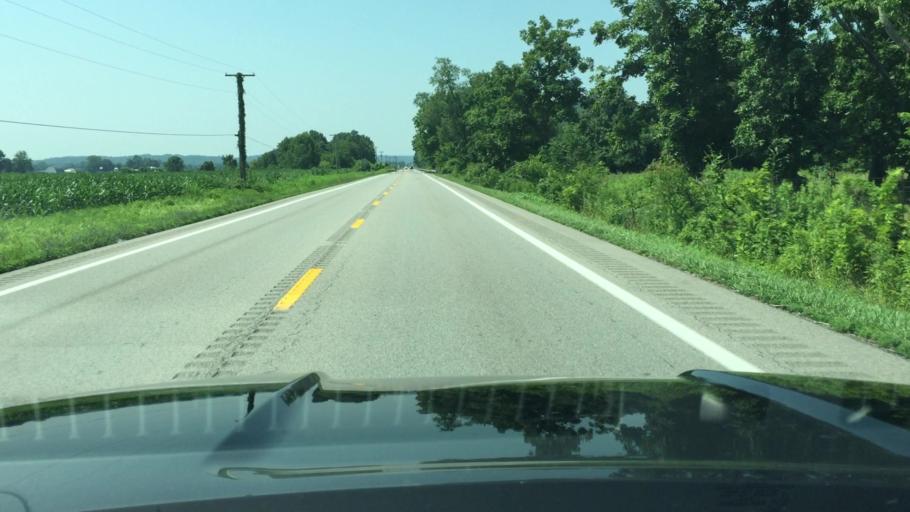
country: US
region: West Virginia
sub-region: Putnam County
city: Buffalo
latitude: 38.6783
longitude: -81.9652
